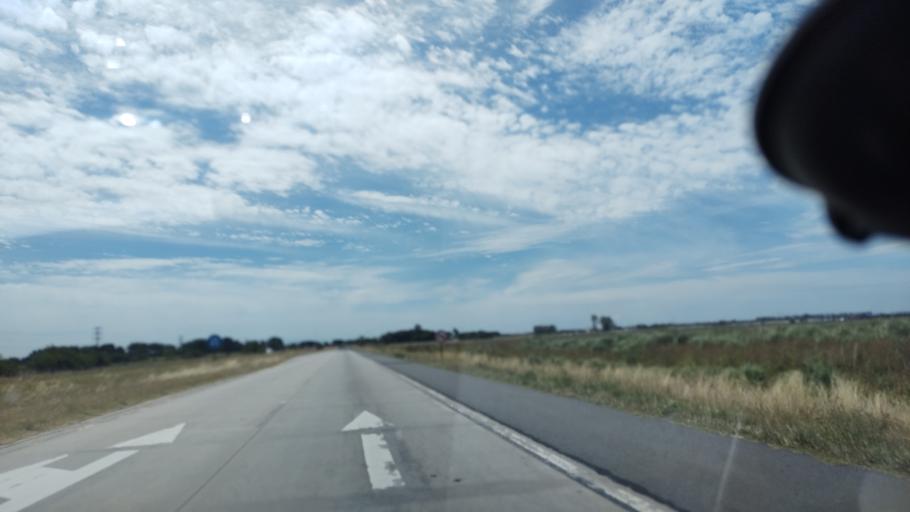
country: AR
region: Buenos Aires
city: Canuelas
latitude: -35.0646
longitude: -58.7024
